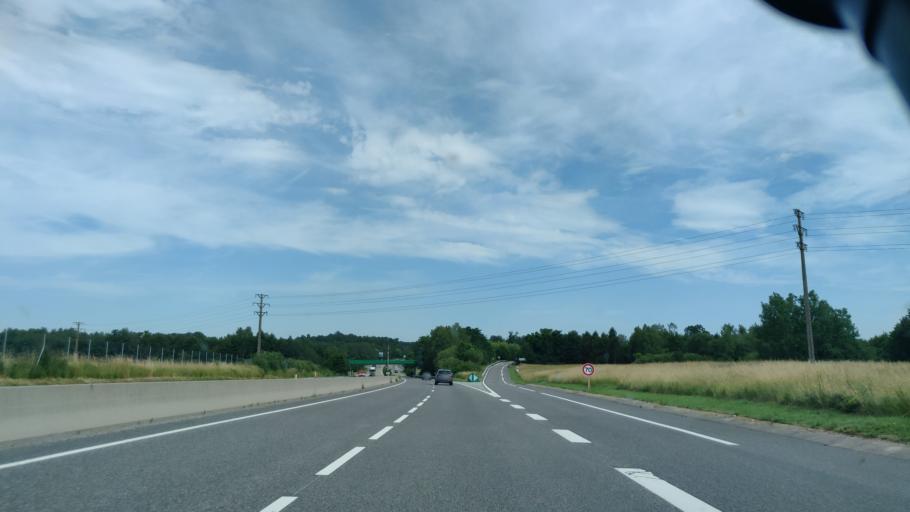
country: FR
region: Lorraine
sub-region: Departement de Meurthe-et-Moselle
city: Baccarat
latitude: 48.4687
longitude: 6.7304
